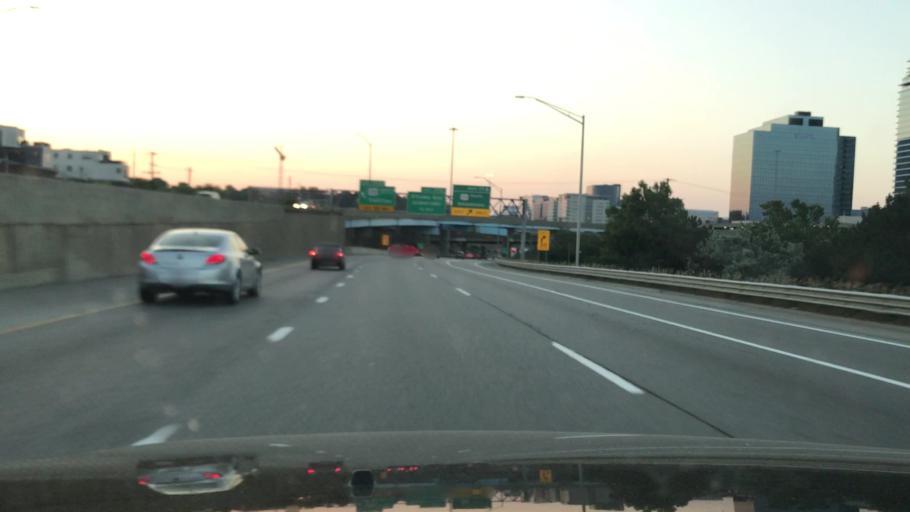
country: US
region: Michigan
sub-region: Kent County
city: Grand Rapids
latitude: 42.9732
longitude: -85.6816
